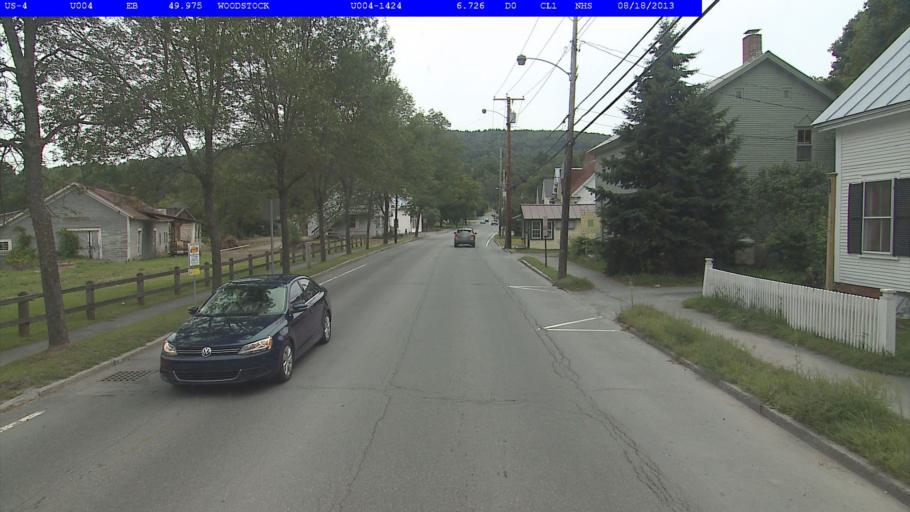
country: US
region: Vermont
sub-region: Windsor County
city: Woodstock
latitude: 43.6267
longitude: -72.5098
